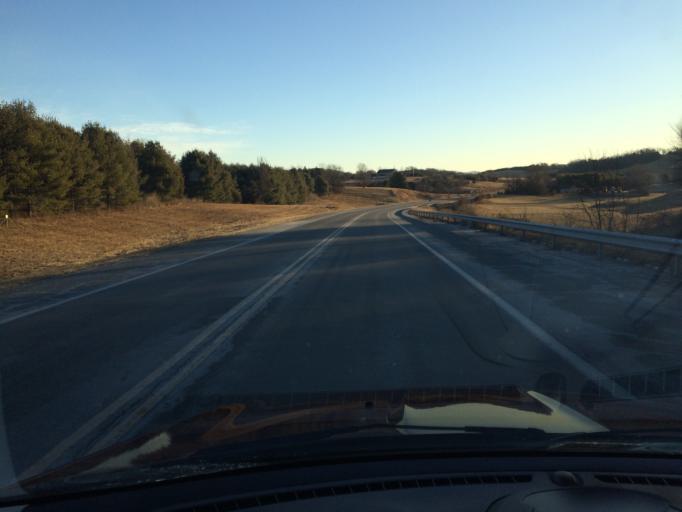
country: US
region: Virginia
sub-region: City of Staunton
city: Staunton
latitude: 38.1869
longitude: -79.0664
